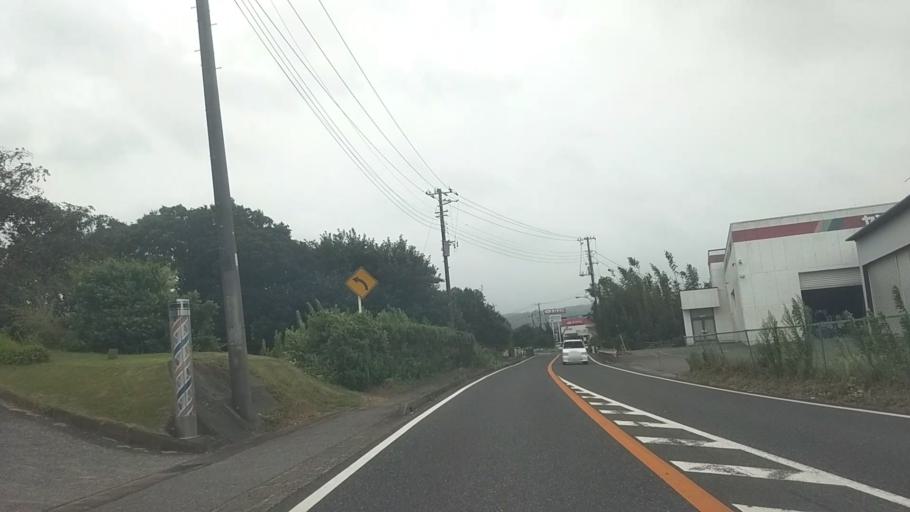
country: JP
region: Chiba
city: Kimitsu
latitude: 35.2180
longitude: 139.8907
